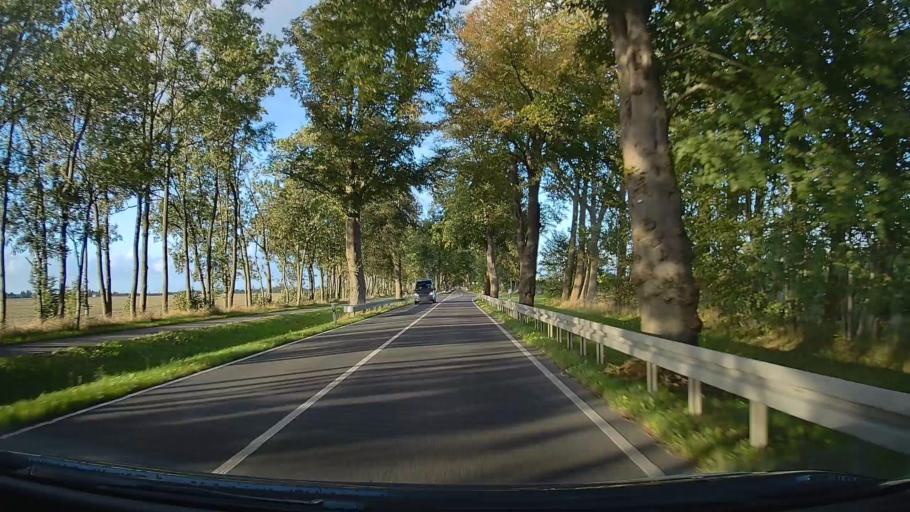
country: DE
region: Mecklenburg-Vorpommern
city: Wendorf
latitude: 54.2731
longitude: 13.0395
